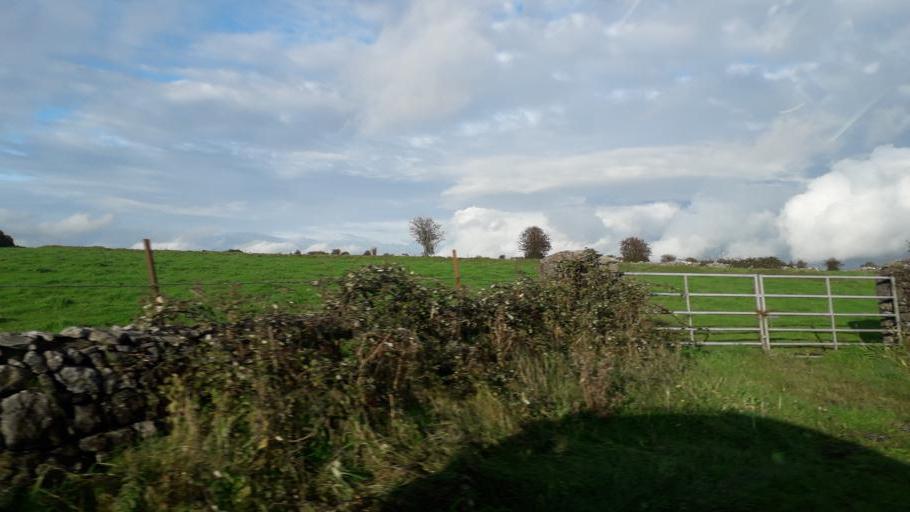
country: IE
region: Connaught
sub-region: Roscommon
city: Roscommon
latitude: 53.7715
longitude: -8.2265
